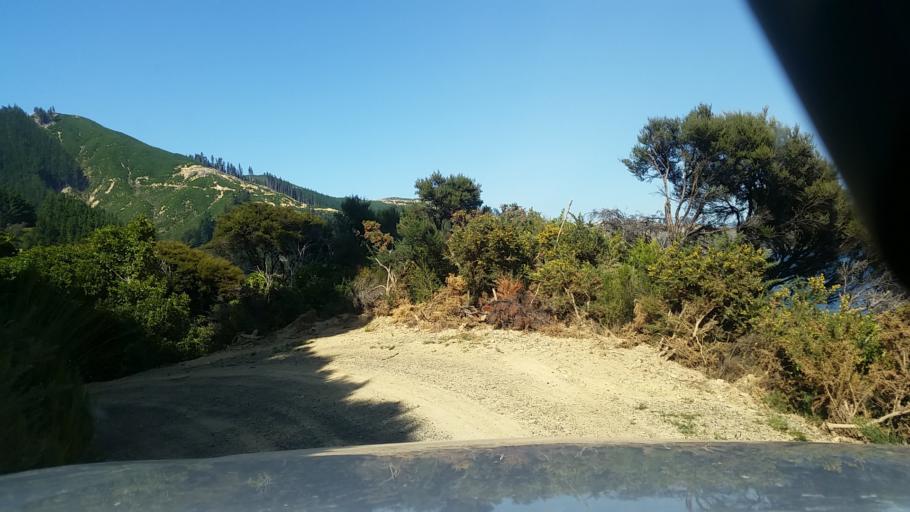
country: NZ
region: Marlborough
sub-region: Marlborough District
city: Picton
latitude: -41.3093
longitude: 174.1711
